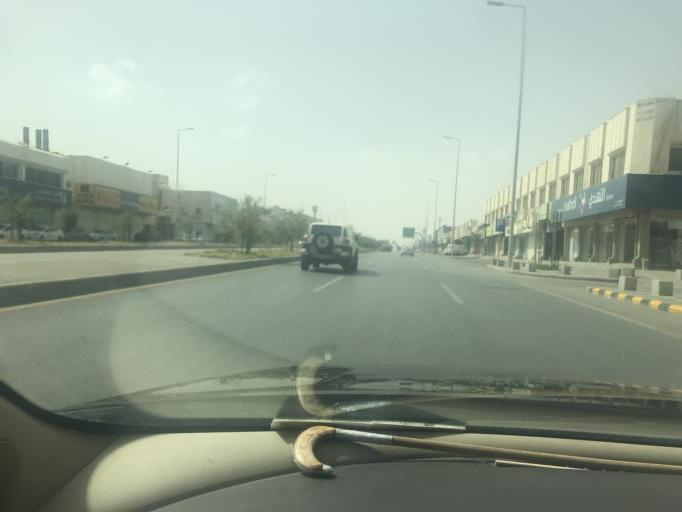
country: SA
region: Ar Riyad
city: Riyadh
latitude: 24.7590
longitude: 46.7657
